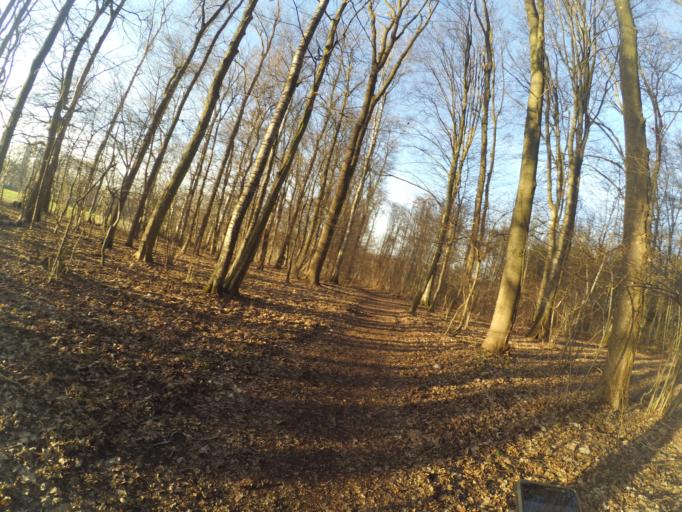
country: DE
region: Bavaria
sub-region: Swabia
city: Guenzburg
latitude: 48.4484
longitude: 10.3017
